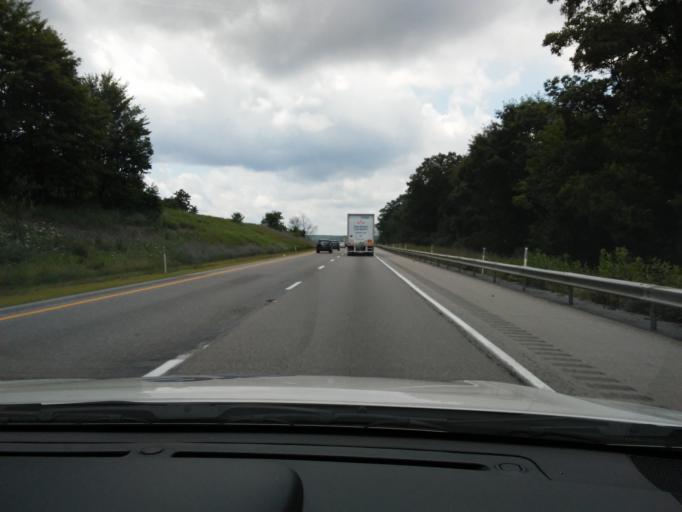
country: US
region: Pennsylvania
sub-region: Centre County
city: Stormstown
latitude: 40.9980
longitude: -77.9974
